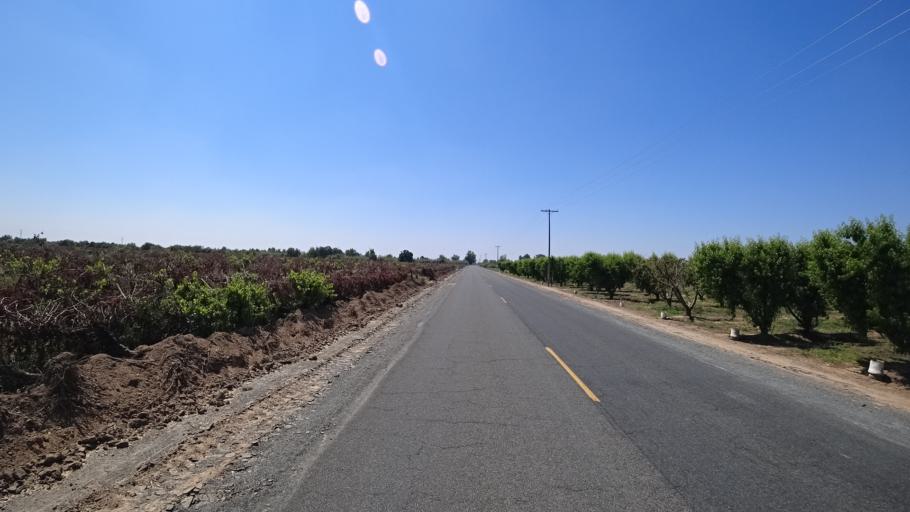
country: US
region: California
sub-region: Fresno County
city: Kingsburg
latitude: 36.4627
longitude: -119.6002
